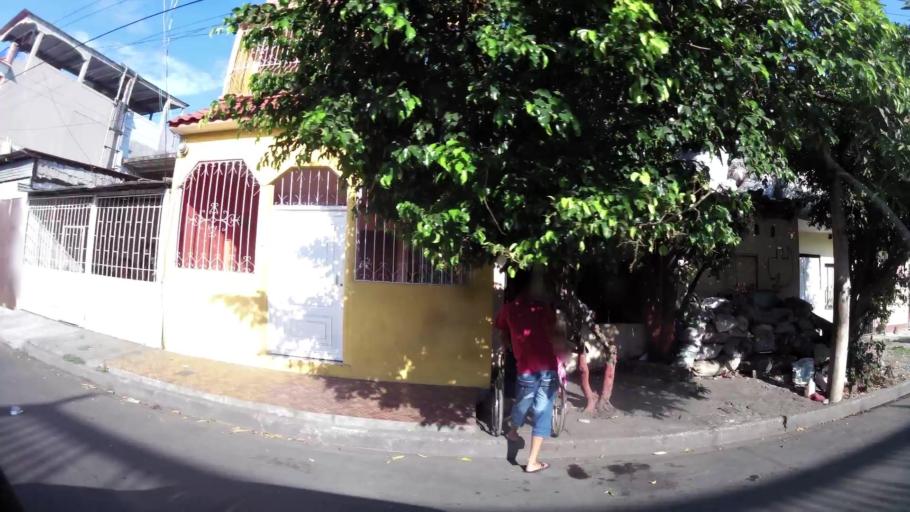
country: EC
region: Guayas
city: Guayaquil
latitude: -2.2146
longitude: -79.9235
